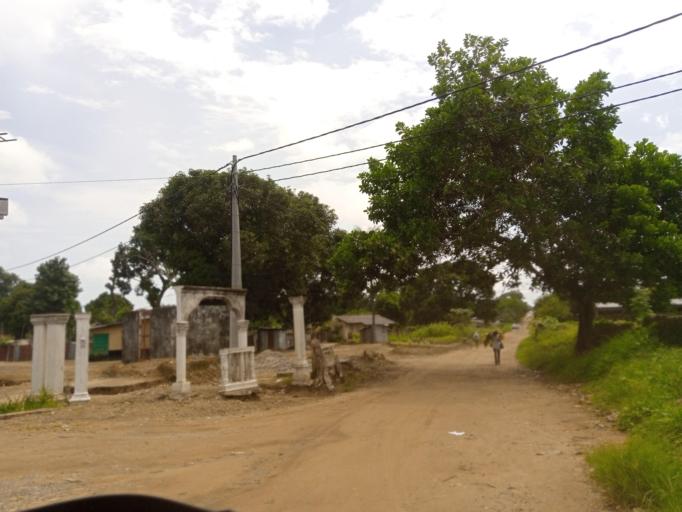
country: SL
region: Northern Province
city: Tintafor
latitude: 8.6251
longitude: -13.2078
